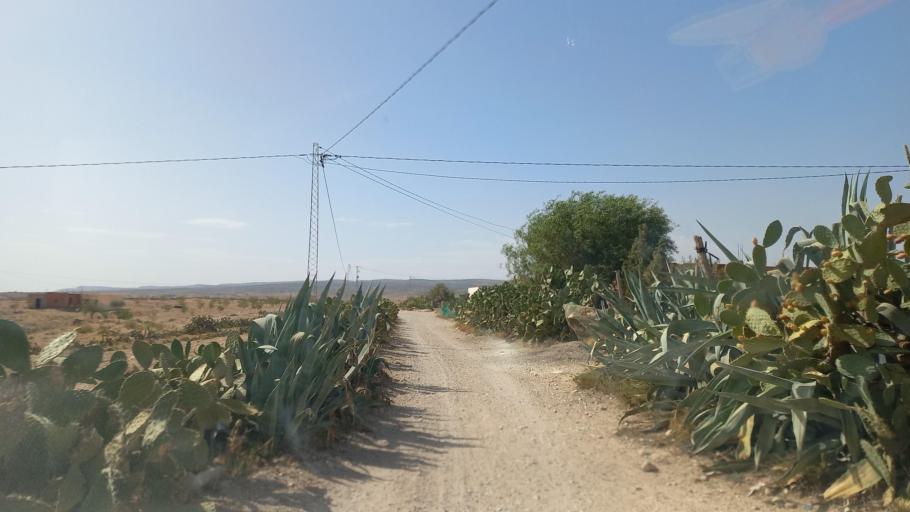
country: TN
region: Al Qasrayn
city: Kasserine
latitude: 35.2713
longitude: 8.9513
